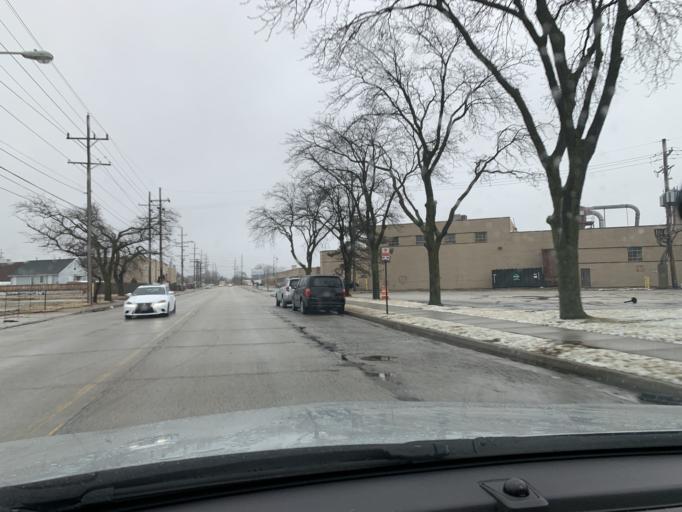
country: US
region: Illinois
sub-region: Cook County
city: Niles
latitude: 42.0172
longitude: -87.7801
